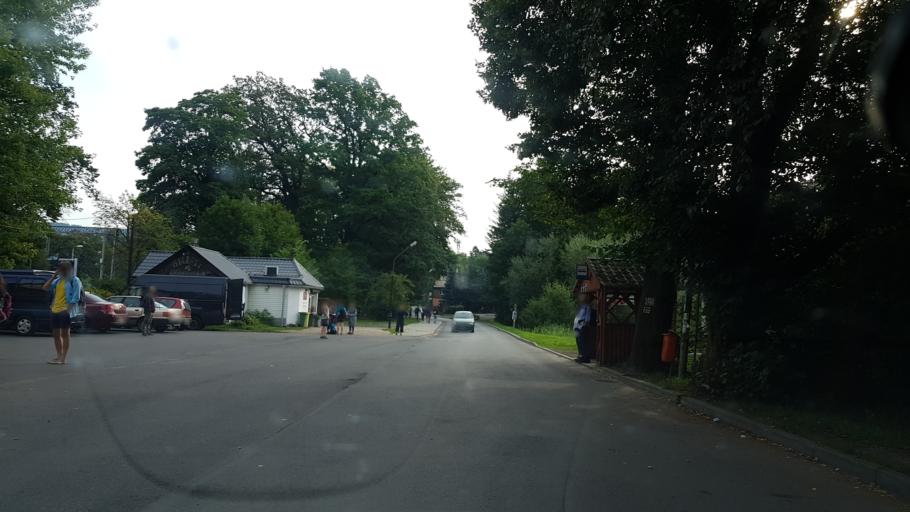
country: PL
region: Lower Silesian Voivodeship
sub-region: Powiat jeleniogorski
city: Janowice Wielkie
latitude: 50.8780
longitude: 15.9189
